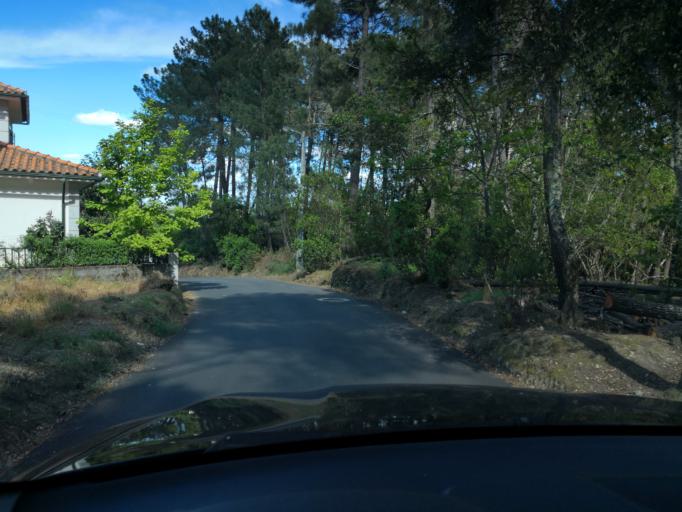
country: PT
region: Vila Real
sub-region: Vila Real
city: Vila Real
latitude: 41.2641
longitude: -7.7317
